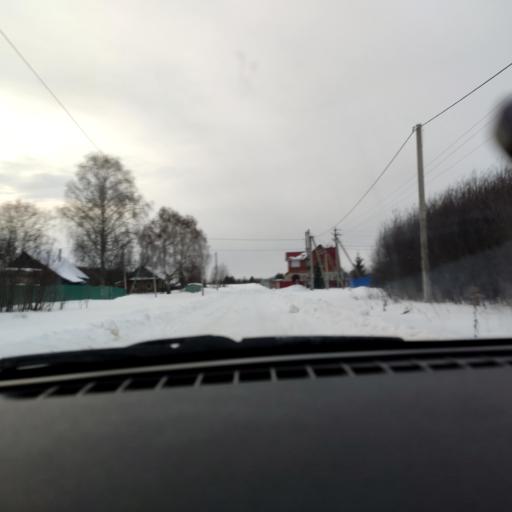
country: RU
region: Bashkortostan
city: Iglino
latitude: 54.7359
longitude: 56.5400
